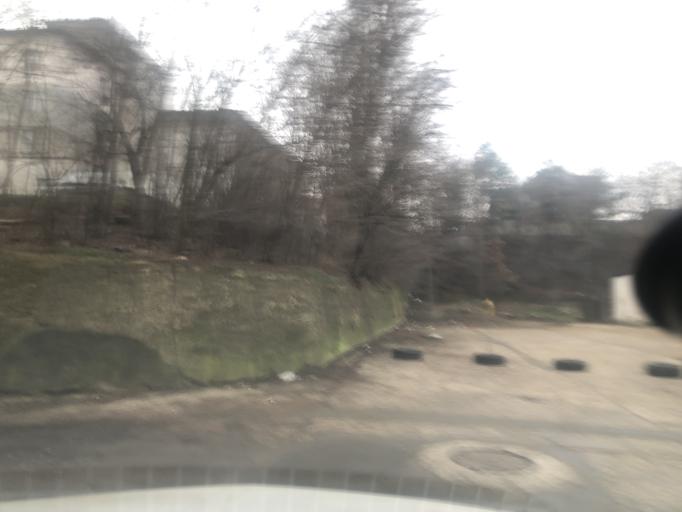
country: MD
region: Chisinau
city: Stauceni
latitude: 47.0657
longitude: 28.8395
